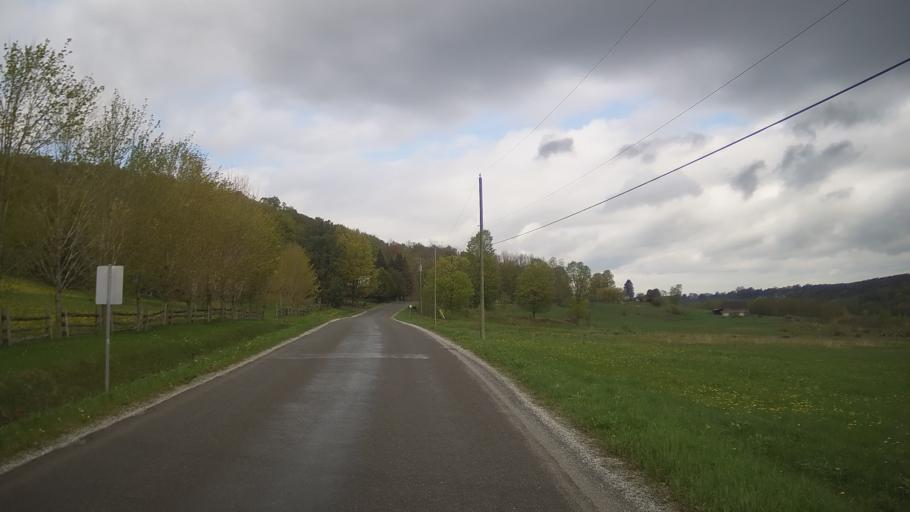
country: CA
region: Quebec
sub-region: Monteregie
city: Cowansville
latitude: 45.1906
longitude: -72.7000
